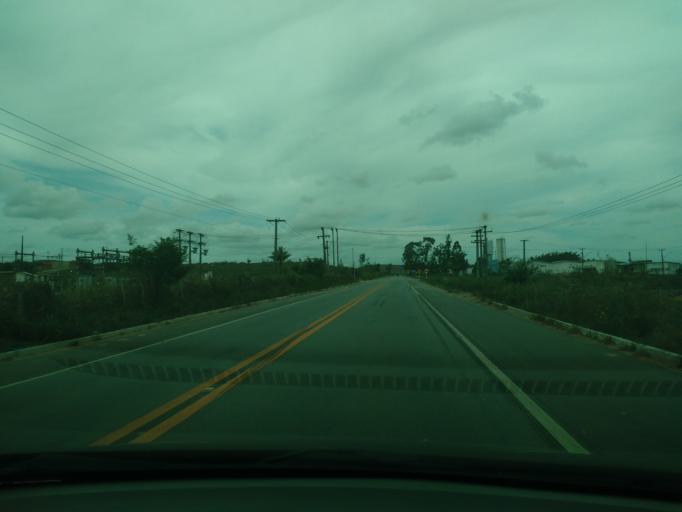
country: BR
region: Alagoas
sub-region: Murici
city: Murici
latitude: -9.3037
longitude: -35.9473
